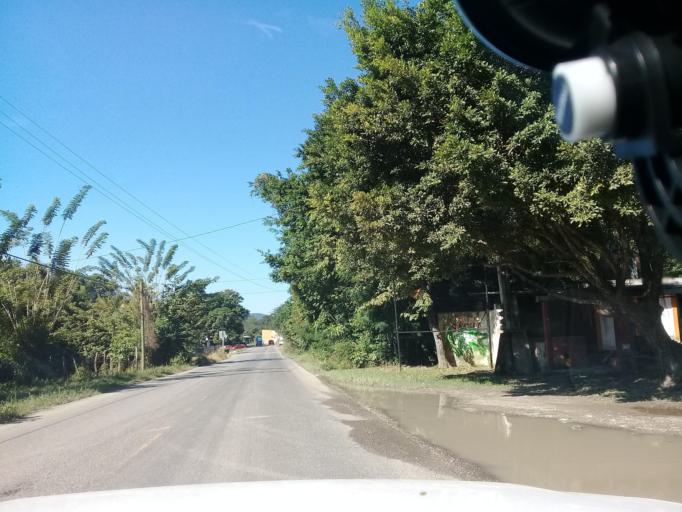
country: MX
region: Hidalgo
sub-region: Huejutla de Reyes
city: Parque de Poblamiento Solidaridad
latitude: 21.1616
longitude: -98.4024
